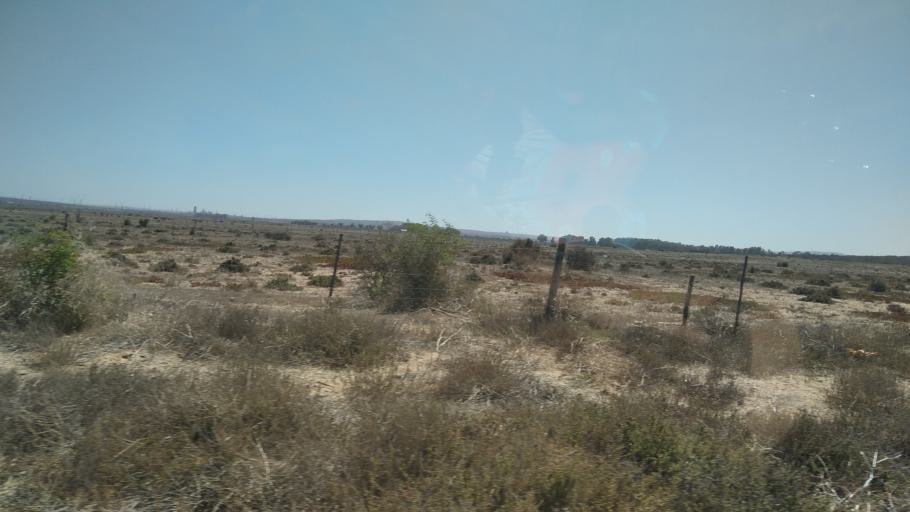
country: ZA
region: Western Cape
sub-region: West Coast District Municipality
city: Vredenburg
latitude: -33.0182
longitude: 18.1117
